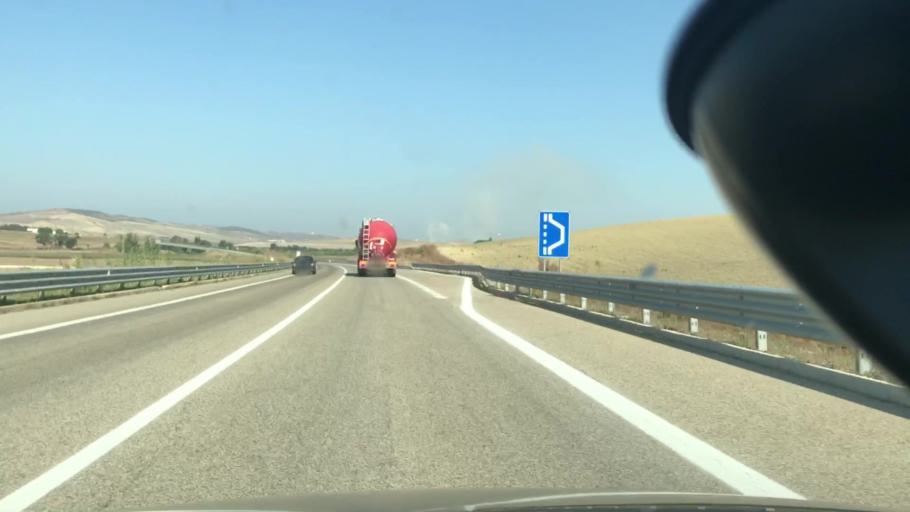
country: IT
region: Basilicate
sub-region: Provincia di Matera
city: Irsina
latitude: 40.7789
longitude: 16.3172
